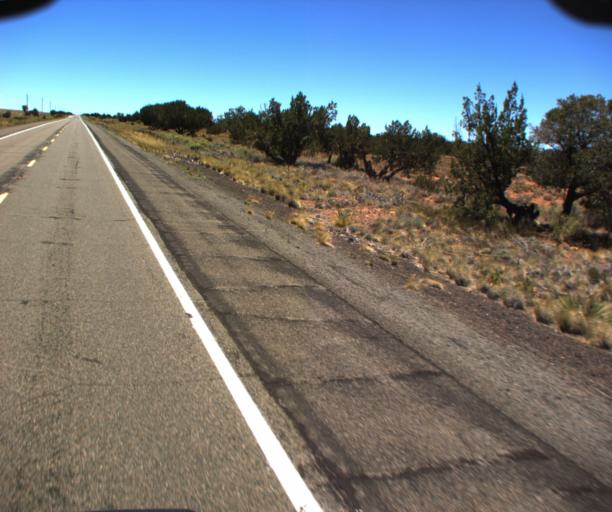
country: US
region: Arizona
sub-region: Coconino County
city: LeChee
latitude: 34.8142
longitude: -110.9681
